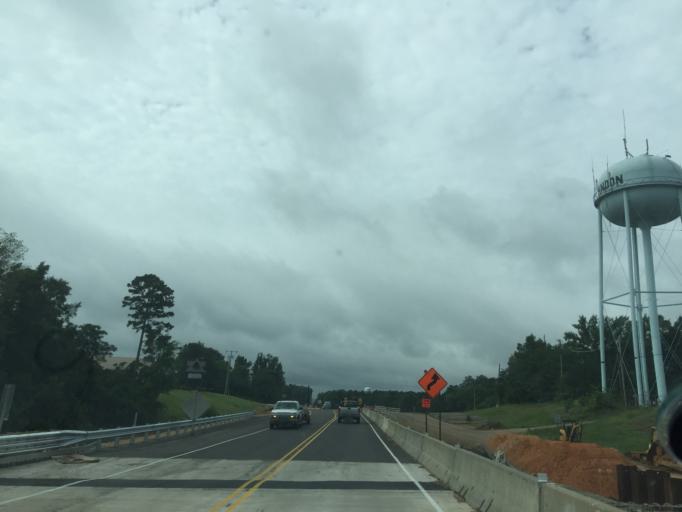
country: US
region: Mississippi
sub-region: Rankin County
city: Brandon
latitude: 32.2789
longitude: -89.9935
